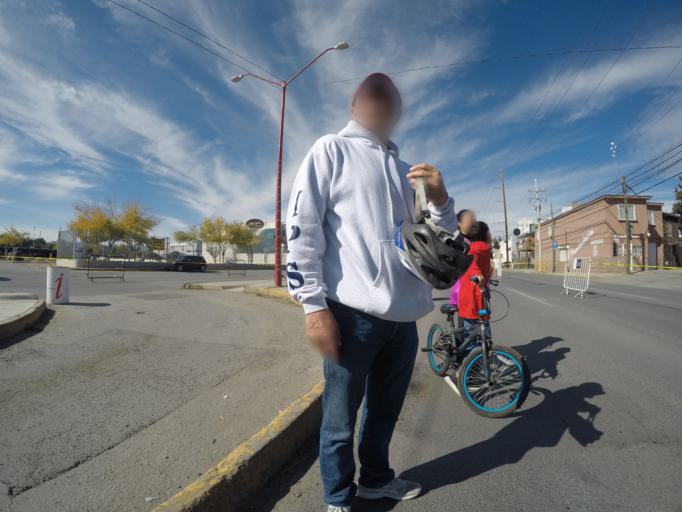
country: MX
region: Chihuahua
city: Ciudad Juarez
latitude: 31.7299
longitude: -106.4092
